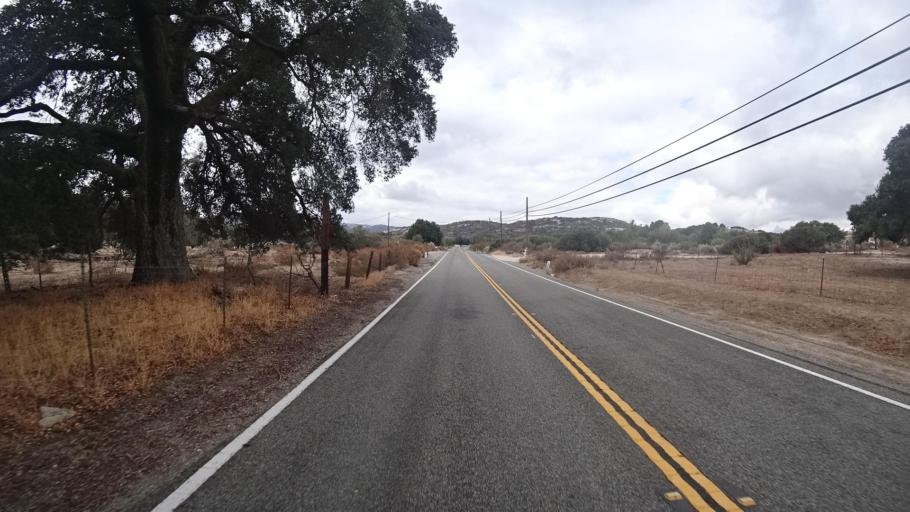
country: US
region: California
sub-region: San Diego County
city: Campo
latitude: 32.6419
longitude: -116.4277
